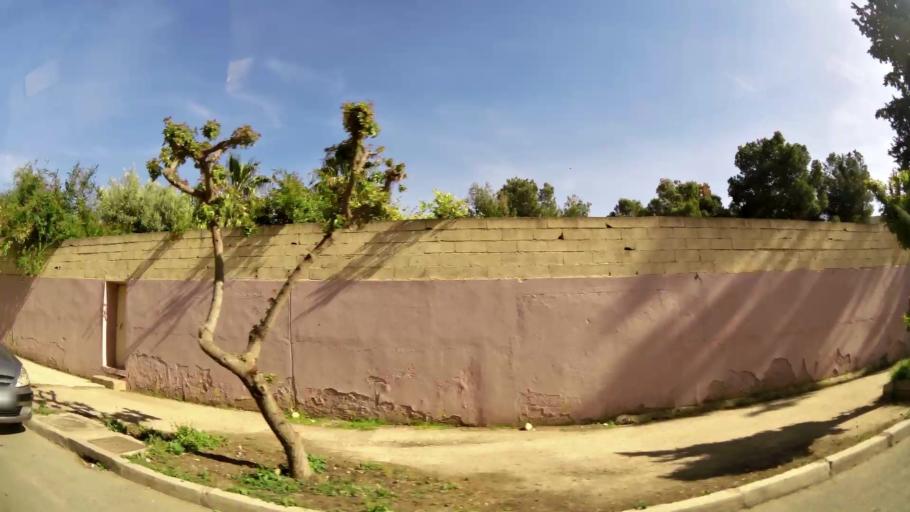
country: MA
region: Oriental
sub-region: Oujda-Angad
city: Oujda
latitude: 34.6706
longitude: -1.9088
